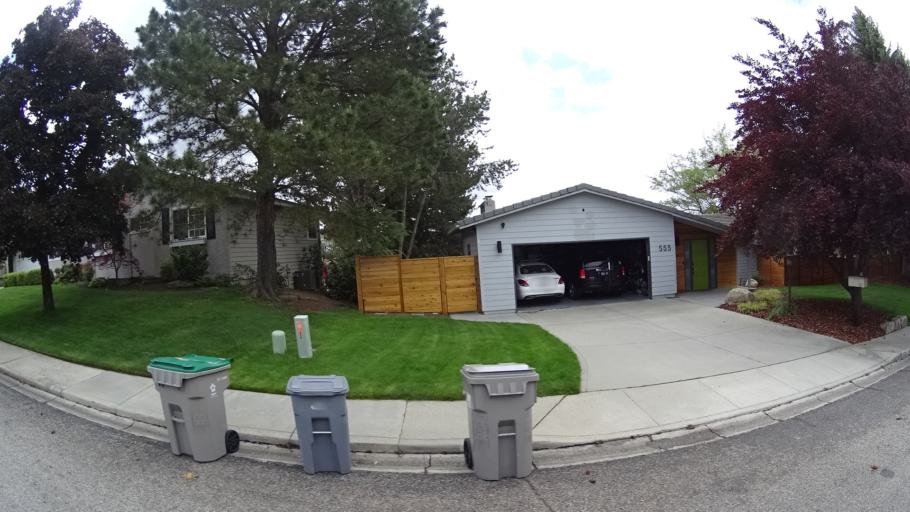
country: US
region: Idaho
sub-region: Ada County
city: Boise
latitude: 43.6512
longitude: -116.1826
